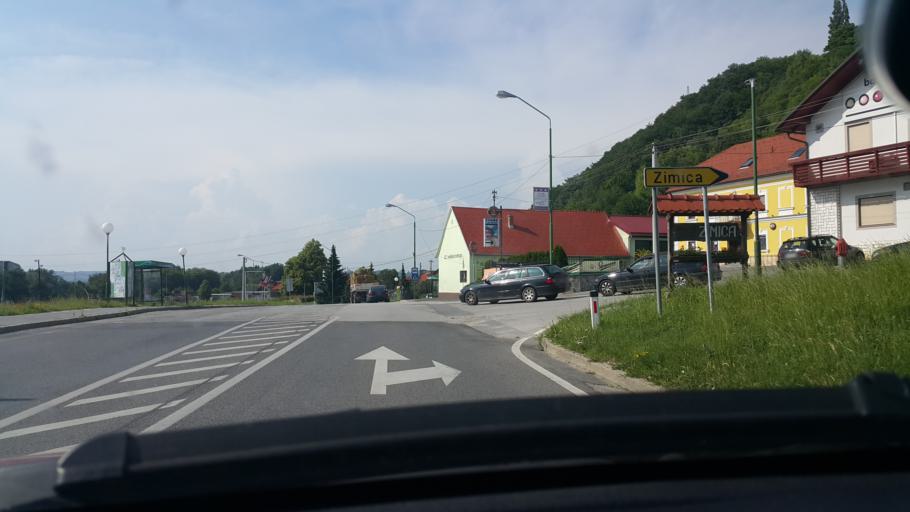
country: SI
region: Duplek
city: Zgornji Duplek
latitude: 46.5139
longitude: 15.7185
